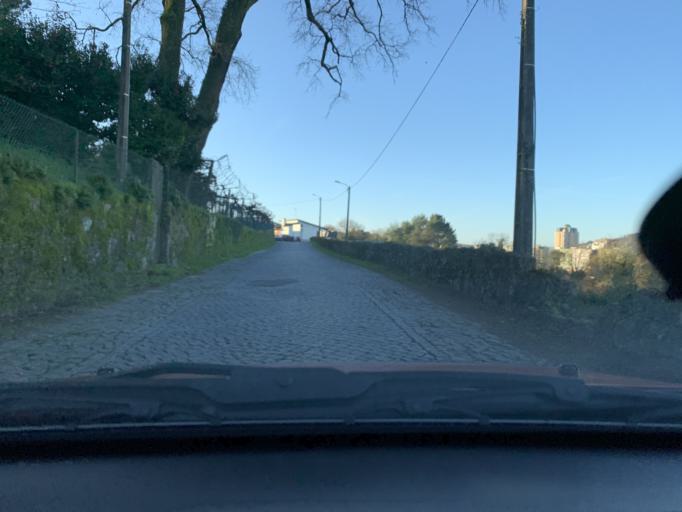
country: PT
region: Braga
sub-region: Vila Nova de Famalicao
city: Vila Nova de Famalicao
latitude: 41.4055
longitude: -8.5103
